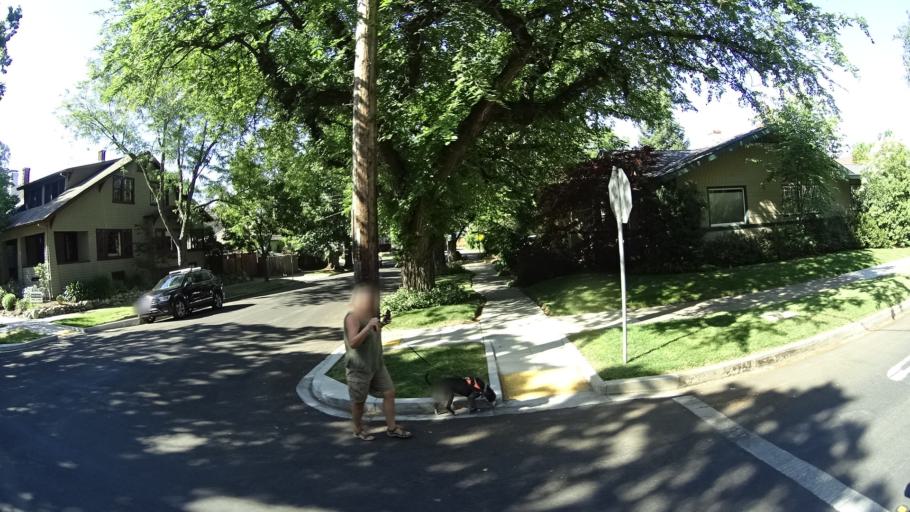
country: US
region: California
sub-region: Sacramento County
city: Sacramento
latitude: 38.5516
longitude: -121.4858
